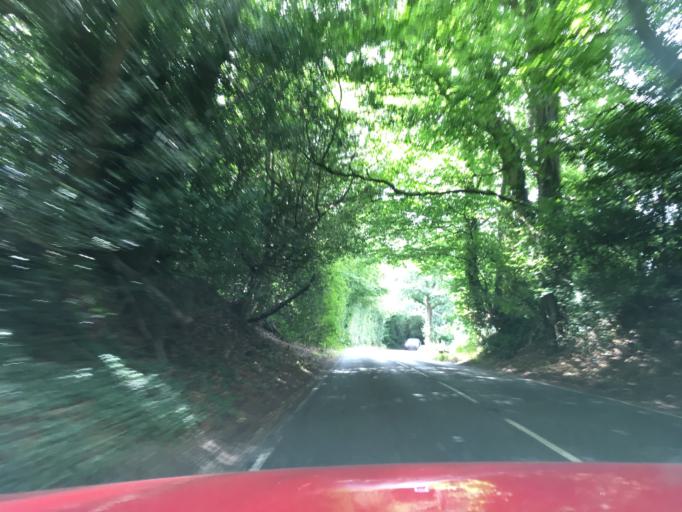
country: GB
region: England
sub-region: West Sussex
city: East Grinstead
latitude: 51.1361
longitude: 0.0148
